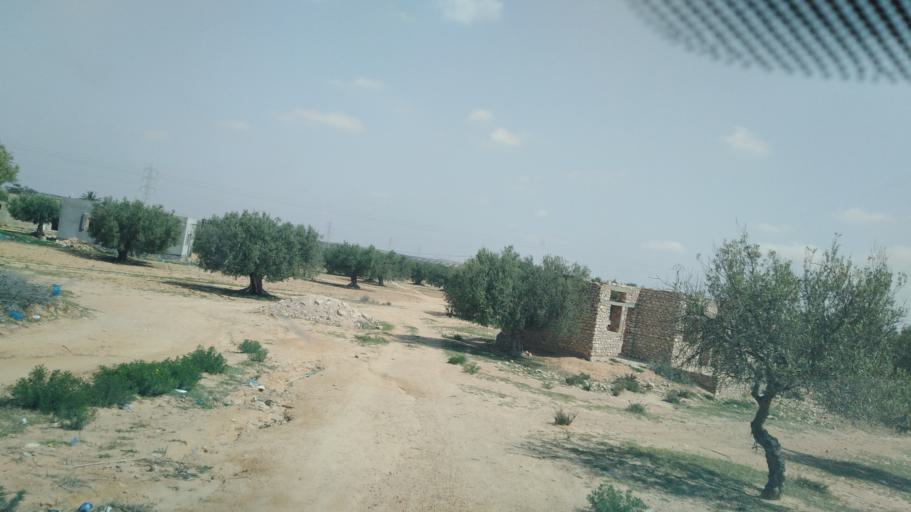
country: TN
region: Safaqis
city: Sfax
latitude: 34.7284
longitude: 10.5656
